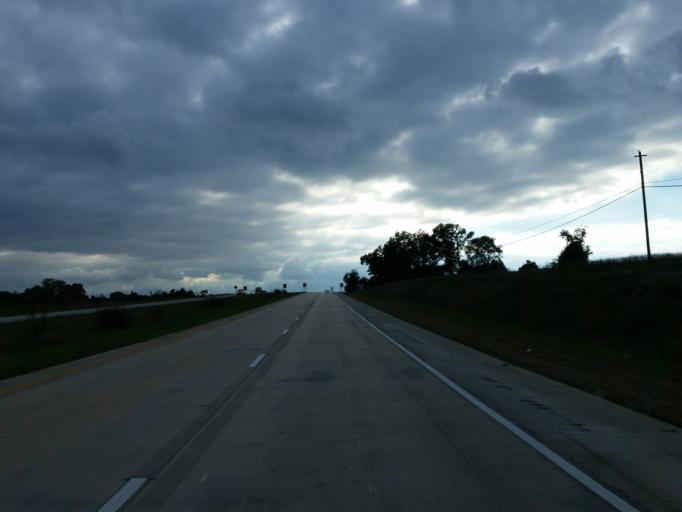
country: US
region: Georgia
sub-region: Bartow County
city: Euharlee
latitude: 34.1129
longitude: -84.8946
